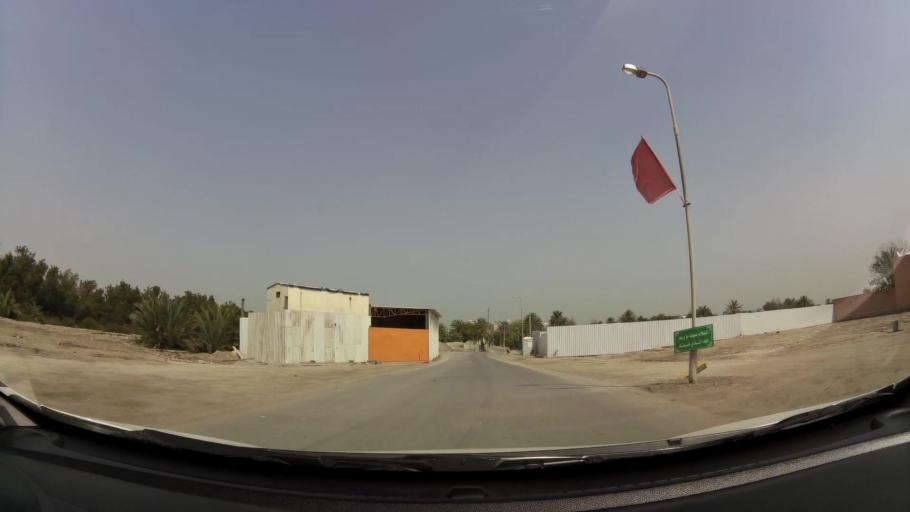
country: BH
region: Manama
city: Jidd Hafs
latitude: 26.2312
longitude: 50.5014
